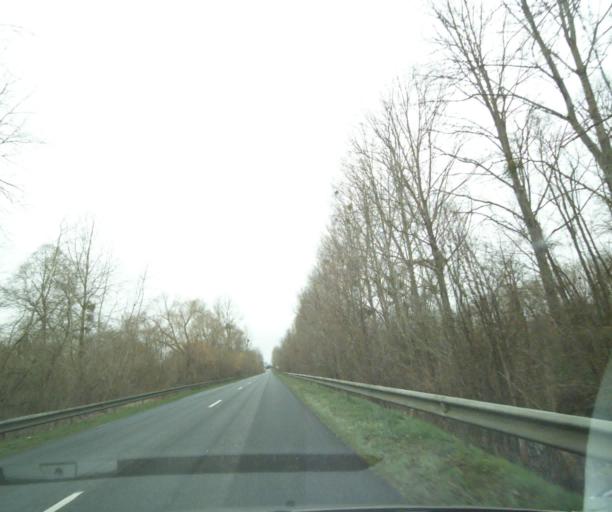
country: FR
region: Picardie
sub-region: Departement de l'Oise
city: Noyon
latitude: 49.5620
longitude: 3.0331
